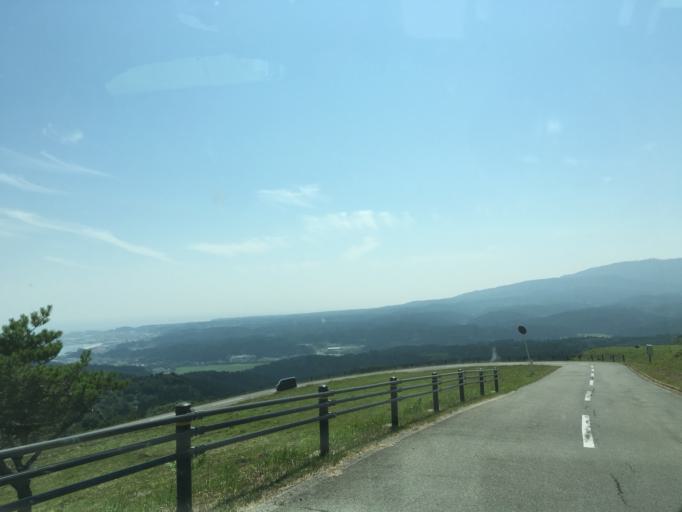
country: JP
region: Akita
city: Tenno
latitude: 39.9287
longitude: 139.8747
